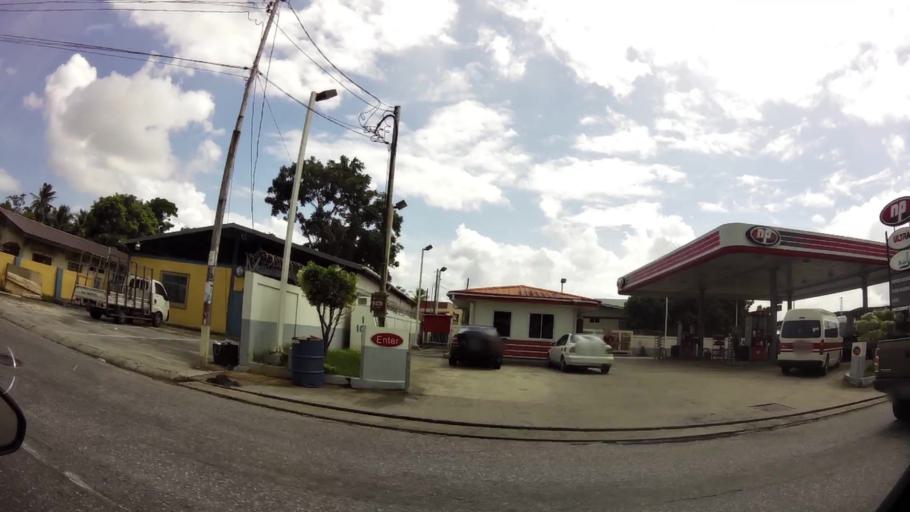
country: TT
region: Borough of Arima
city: Arima
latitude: 10.6363
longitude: -61.2889
